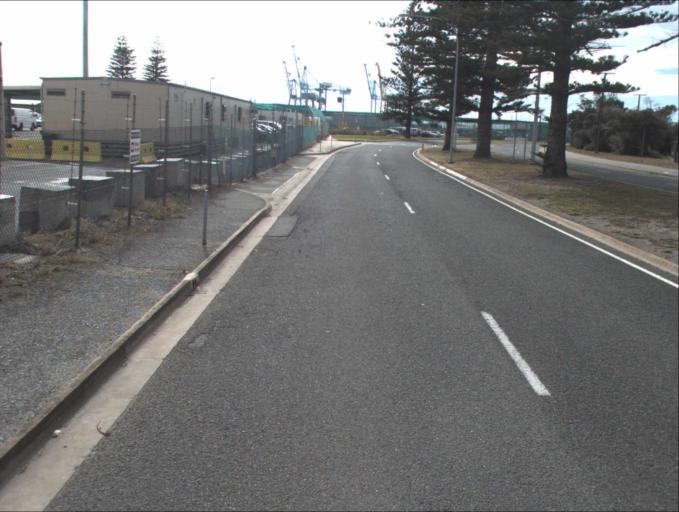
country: AU
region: South Australia
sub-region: Port Adelaide Enfield
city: Birkenhead
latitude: -34.7777
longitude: 138.4842
